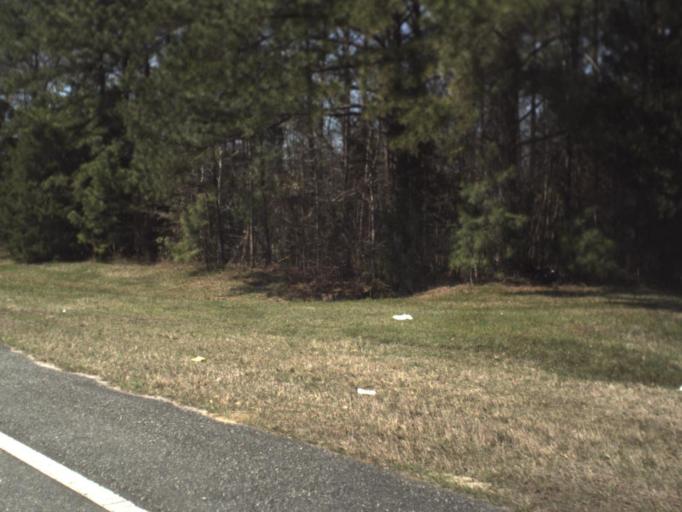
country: US
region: Florida
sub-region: Jackson County
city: Marianna
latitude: 30.7513
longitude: -85.2771
